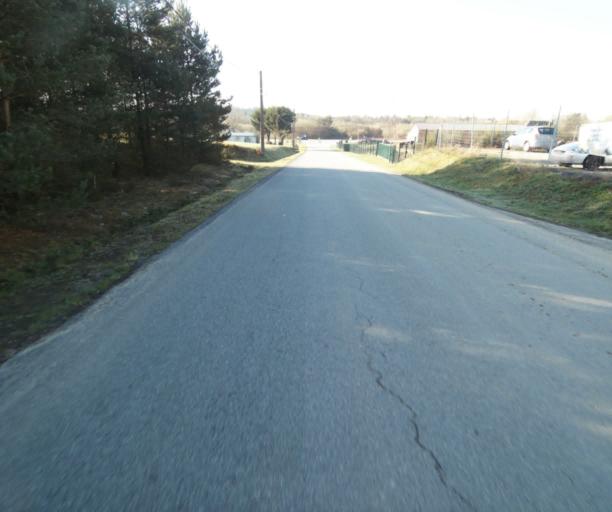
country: FR
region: Limousin
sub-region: Departement de la Correze
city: Correze
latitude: 45.3359
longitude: 1.9145
